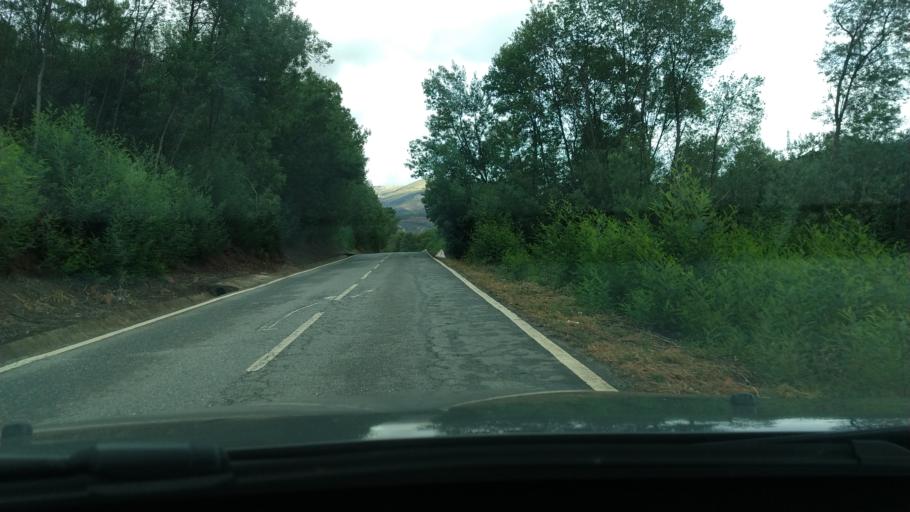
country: PT
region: Castelo Branco
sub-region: Covilha
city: Covilha
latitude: 40.2276
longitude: -7.6086
